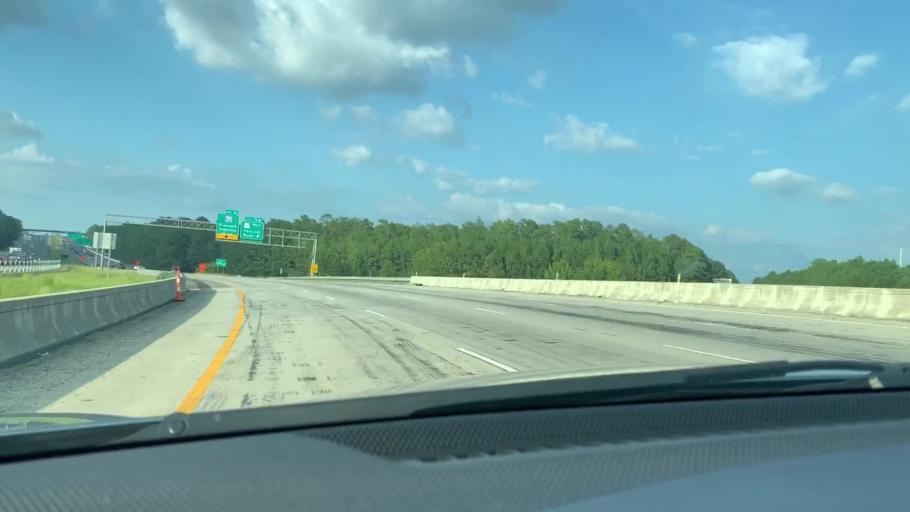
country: US
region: South Carolina
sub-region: Richland County
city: Woodfield
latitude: 34.0521
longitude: -80.9230
